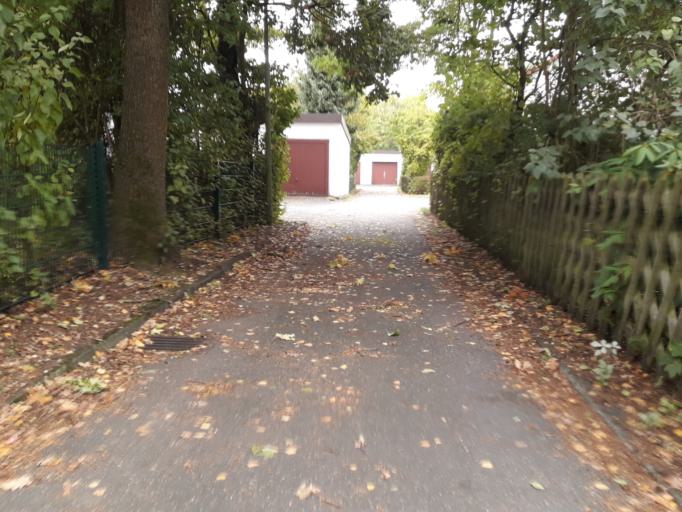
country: DE
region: North Rhine-Westphalia
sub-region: Regierungsbezirk Detmold
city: Paderborn
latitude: 51.7596
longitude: 8.7272
